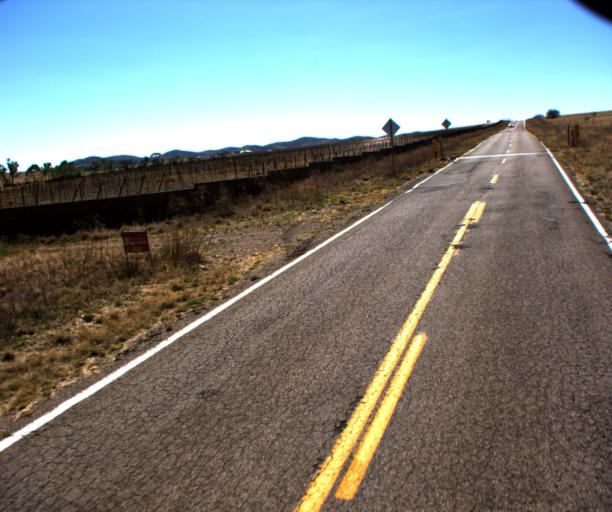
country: US
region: Arizona
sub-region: Cochise County
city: Huachuca City
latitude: 31.6007
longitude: -110.5628
